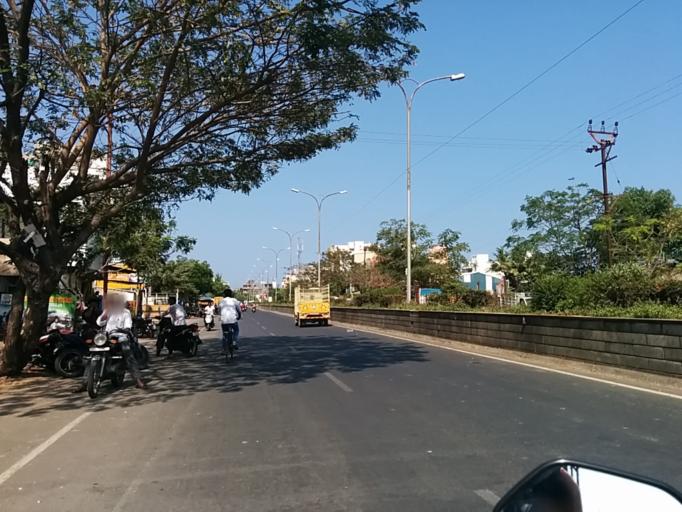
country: IN
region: Pondicherry
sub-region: Puducherry
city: Puducherry
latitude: 11.9489
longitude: 79.8136
